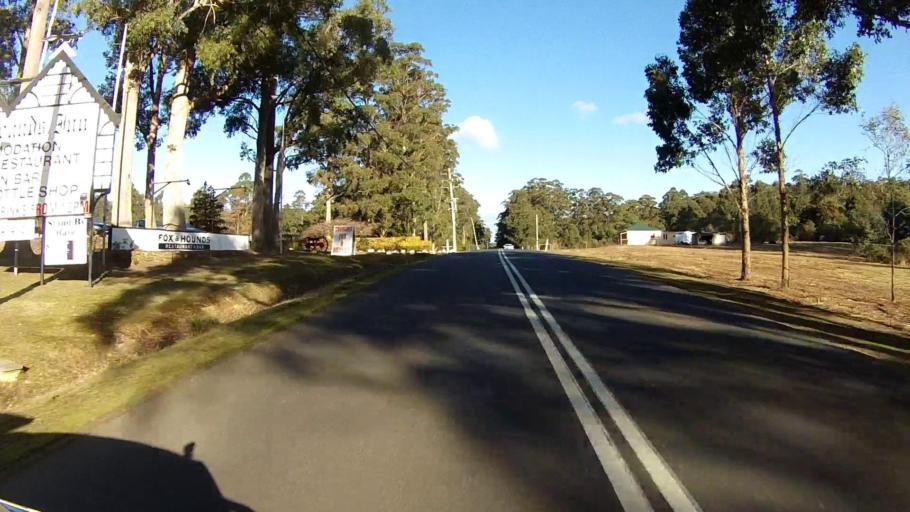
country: AU
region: Tasmania
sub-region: Clarence
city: Sandford
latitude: -43.1248
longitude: 147.8501
